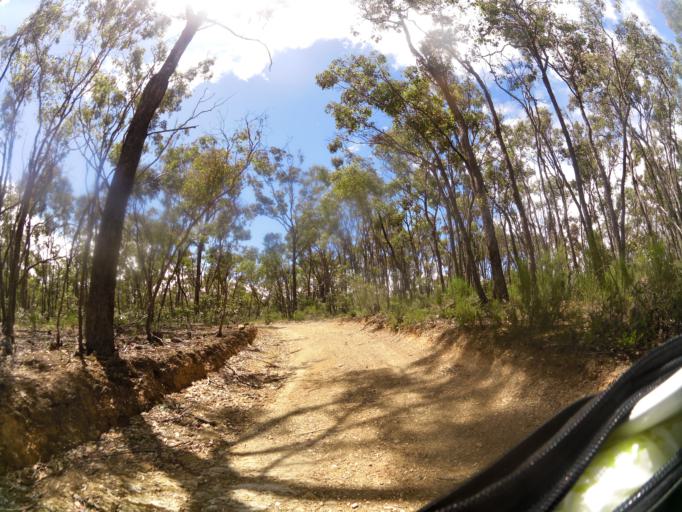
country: AU
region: Victoria
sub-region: Mount Alexander
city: Castlemaine
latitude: -37.0719
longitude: 144.2610
